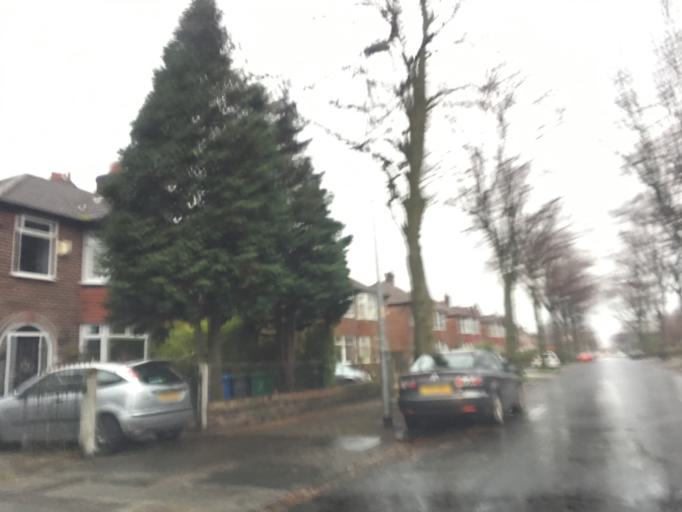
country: GB
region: England
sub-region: Manchester
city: Chorlton cum Hardy
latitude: 53.4248
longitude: -2.2620
